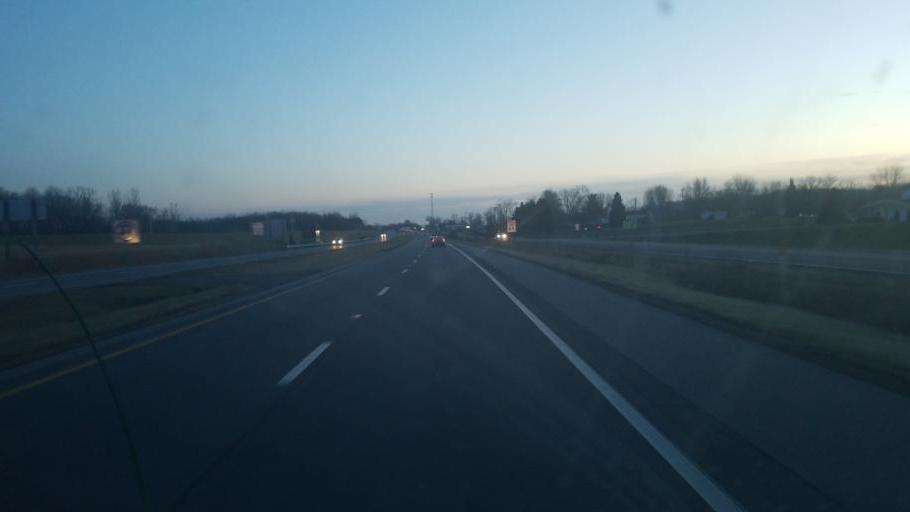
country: US
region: Ohio
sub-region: Marion County
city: Prospect
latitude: 40.4532
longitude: -83.0752
